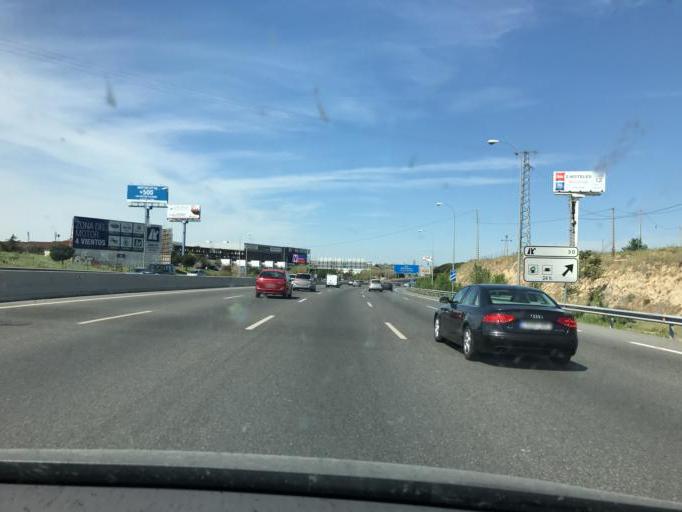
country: ES
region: Madrid
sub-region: Provincia de Madrid
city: Leganes
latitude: 40.3596
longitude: -3.7716
